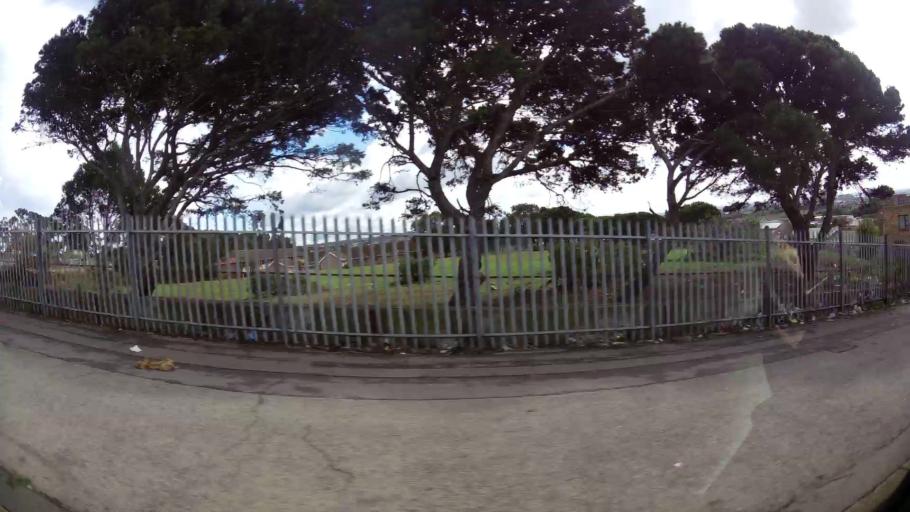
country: ZA
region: Eastern Cape
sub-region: Nelson Mandela Bay Metropolitan Municipality
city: Port Elizabeth
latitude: -33.9303
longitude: 25.5681
